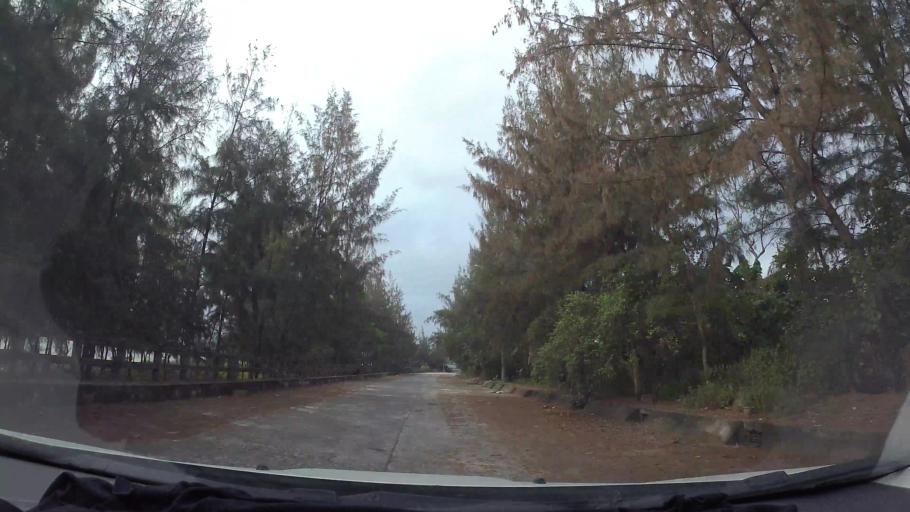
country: VN
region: Da Nang
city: Lien Chieu
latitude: 16.1248
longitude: 108.1237
